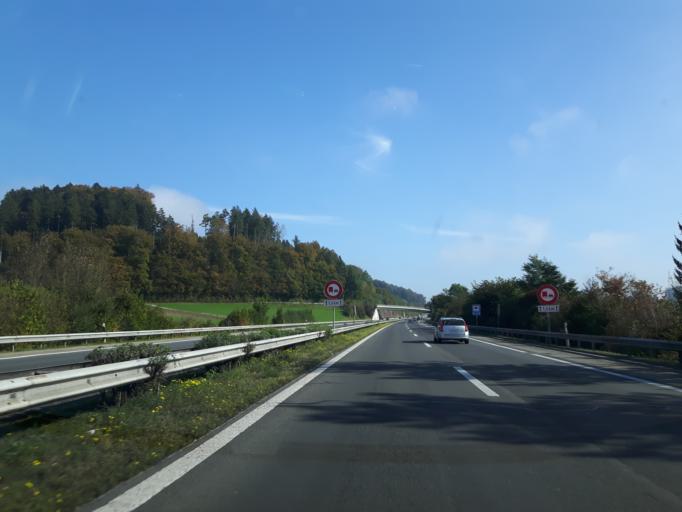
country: CH
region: Lucerne
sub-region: Sursee District
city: Knutwil
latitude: 47.2014
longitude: 8.0528
